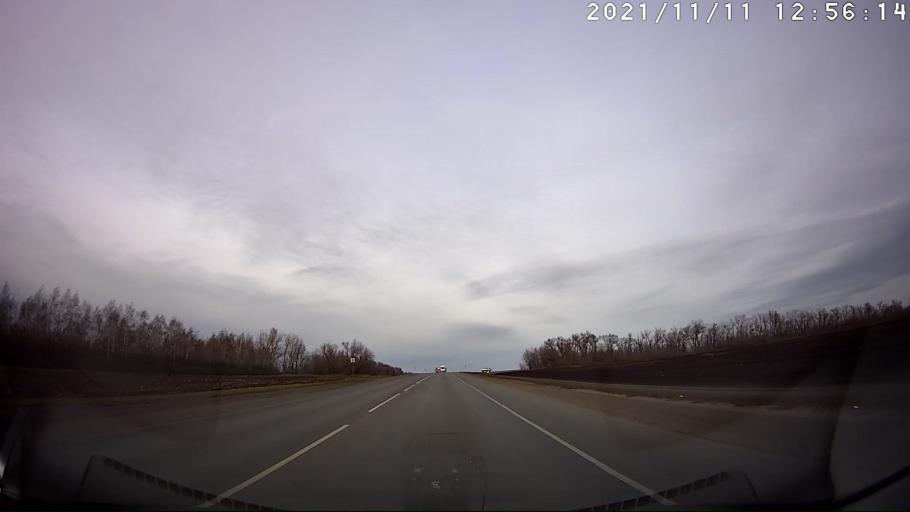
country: RU
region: Ulyanovsk
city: Isheyevka
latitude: 54.3161
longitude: 48.2330
